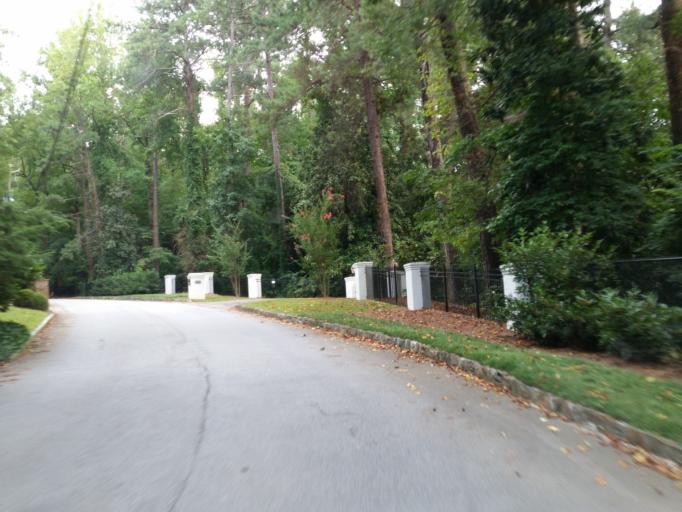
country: US
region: Georgia
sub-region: Cobb County
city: Vinings
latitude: 33.8557
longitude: -84.4439
